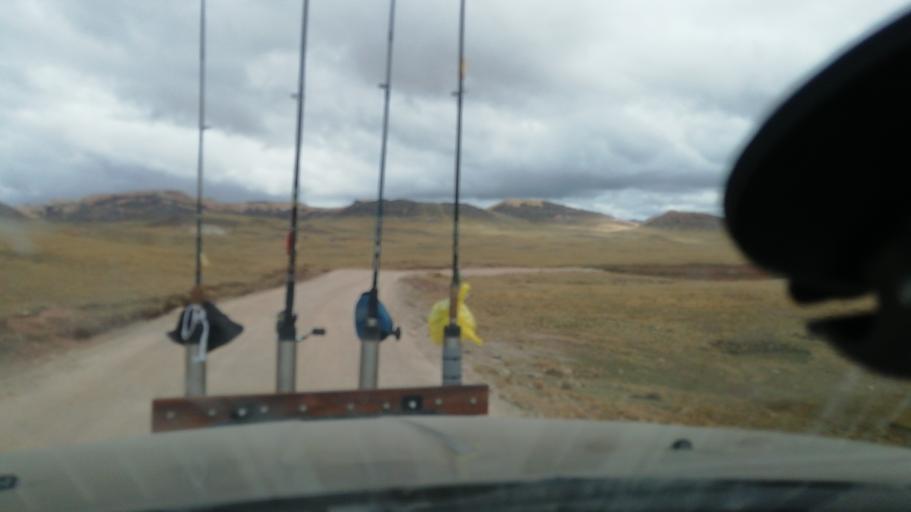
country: PE
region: Huancavelica
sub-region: Provincia de Huancavelica
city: Acobambilla
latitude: -12.5453
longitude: -75.5468
